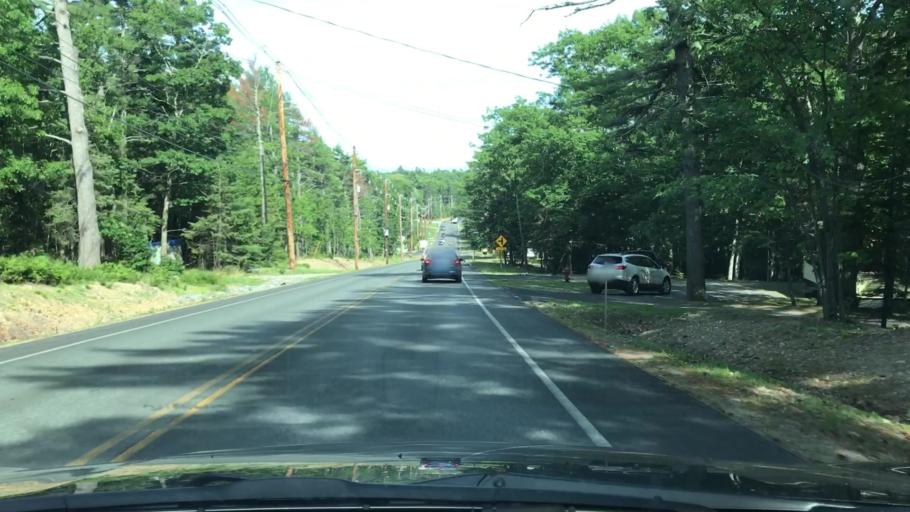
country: US
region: Maine
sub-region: Hancock County
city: Bar Harbor
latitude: 44.4301
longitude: -68.2611
